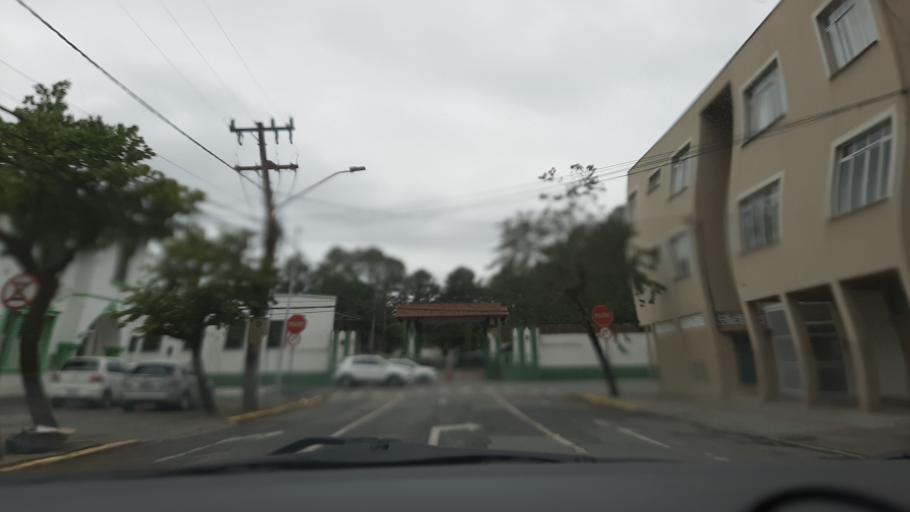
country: BR
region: Santa Catarina
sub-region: Joinville
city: Joinville
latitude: -26.3065
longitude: -48.8513
